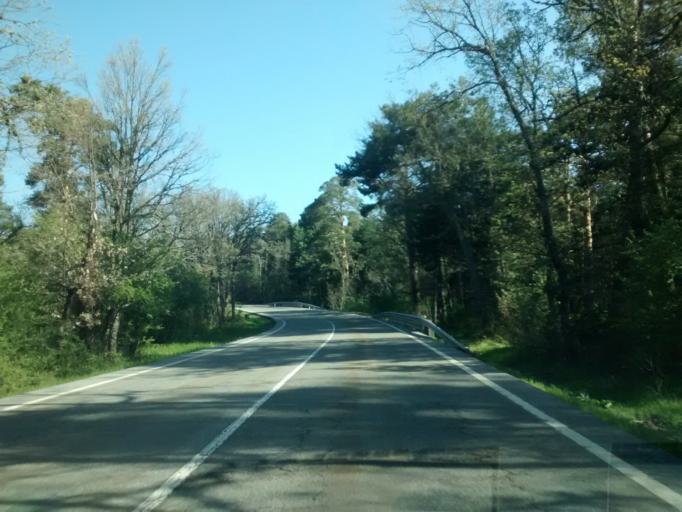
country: ES
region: Castille and Leon
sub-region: Provincia de Segovia
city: San Ildefonso
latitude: 40.8623
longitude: -4.0264
